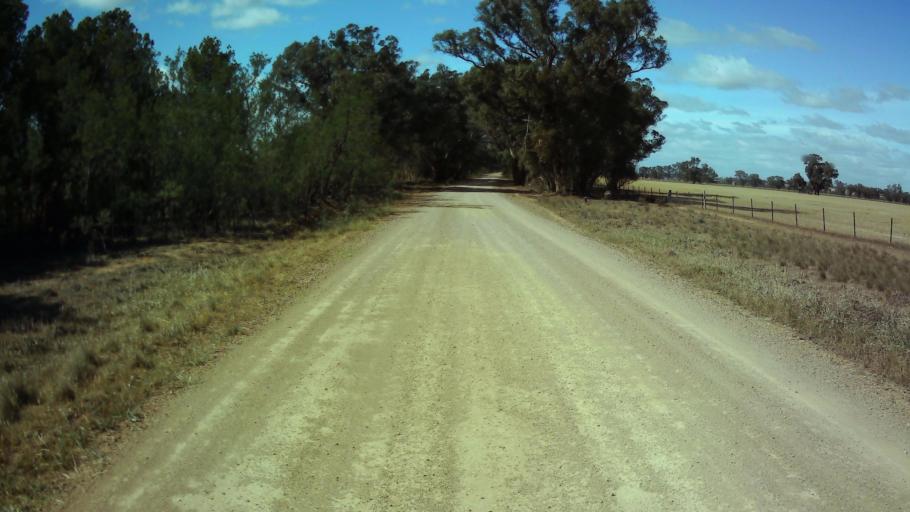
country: AU
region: New South Wales
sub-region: Weddin
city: Grenfell
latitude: -34.0357
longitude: 148.3167
